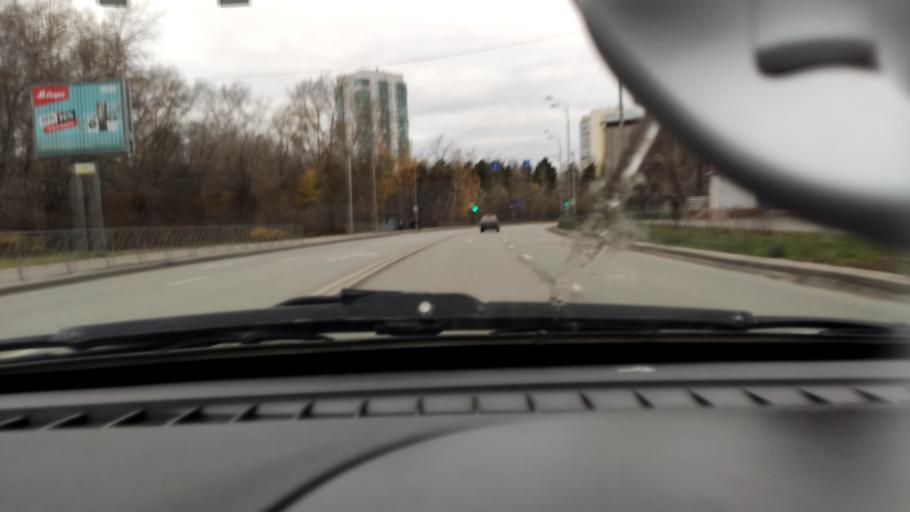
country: RU
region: Perm
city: Perm
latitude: 57.9921
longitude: 56.1898
